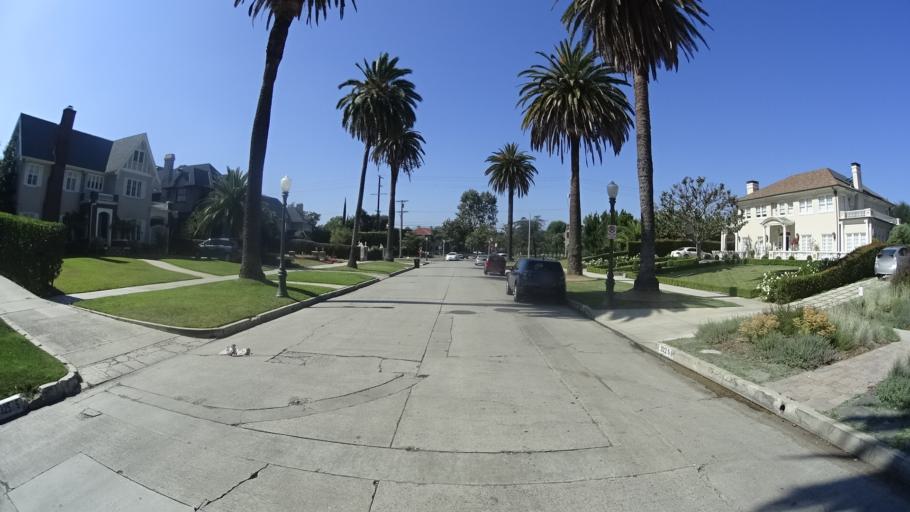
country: US
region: California
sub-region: Los Angeles County
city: Hollywood
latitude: 34.0682
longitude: -118.3229
